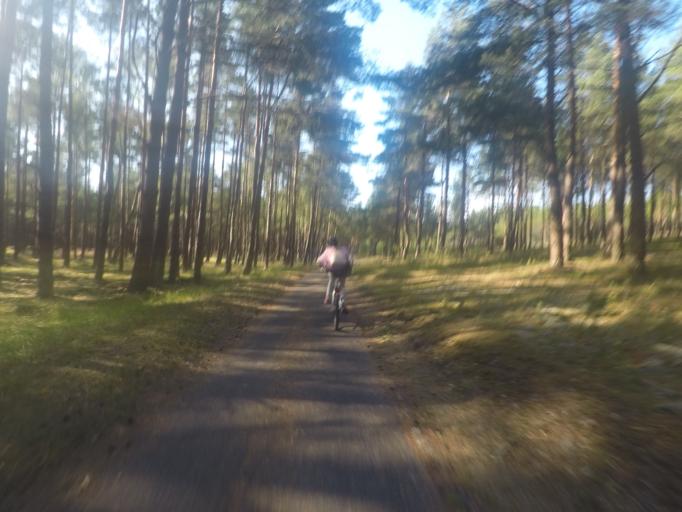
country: LT
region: Klaipedos apskritis
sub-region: Klaipeda
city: Klaipeda
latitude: 55.5796
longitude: 21.1139
